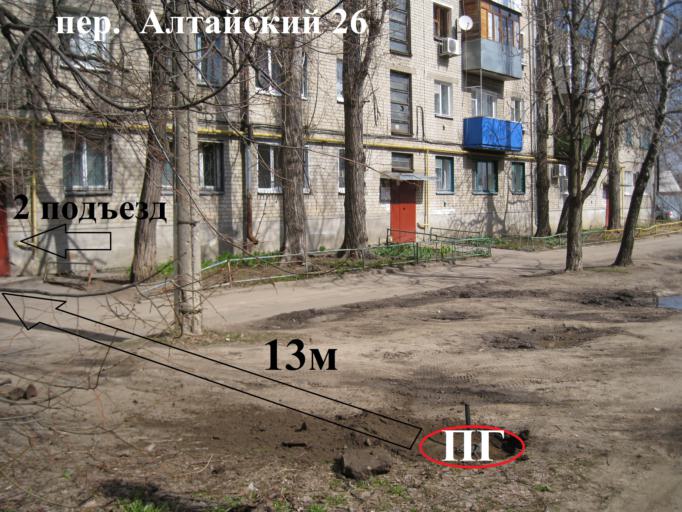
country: RU
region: Voronezj
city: Voronezh
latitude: 51.6453
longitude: 39.2019
